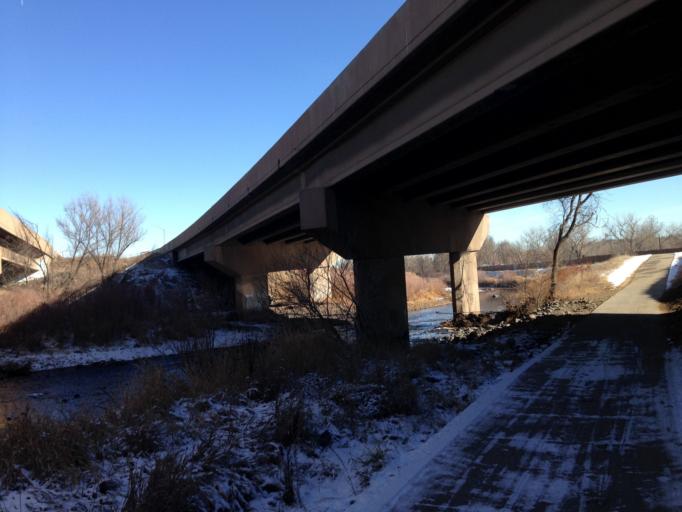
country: US
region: Colorado
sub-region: Adams County
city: Berkley
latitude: 39.7971
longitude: -105.0482
